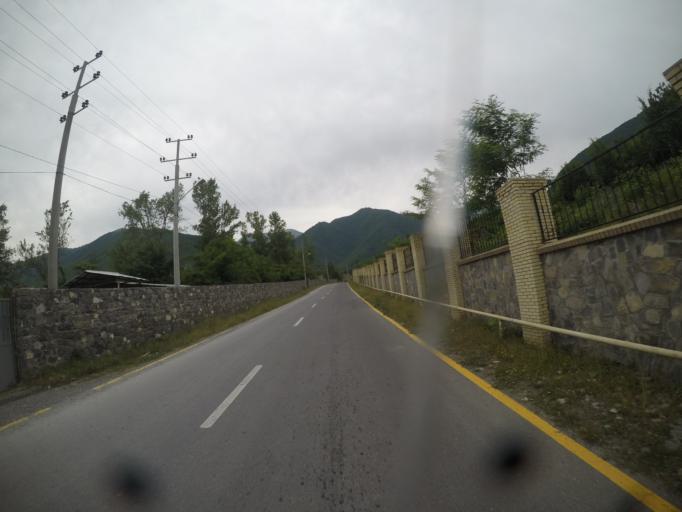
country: AZ
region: Shaki City
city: Sheki
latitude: 41.2470
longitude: 47.2013
